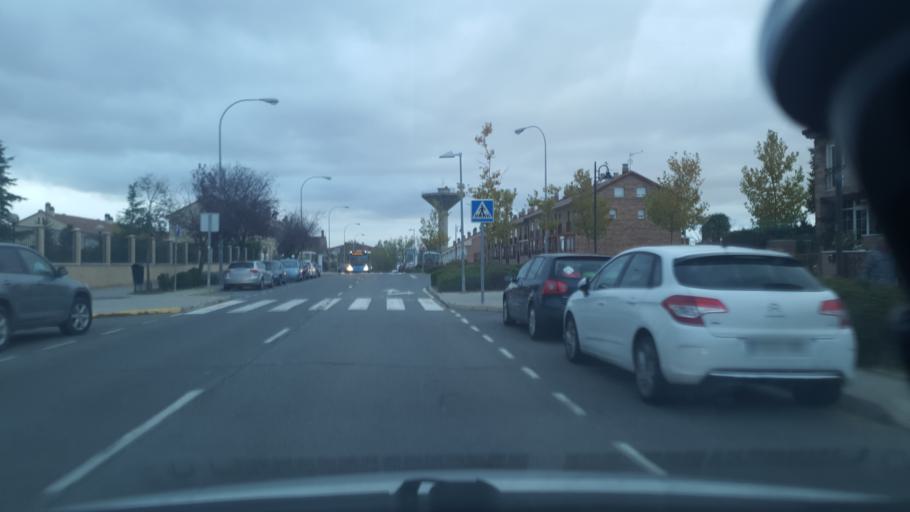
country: ES
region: Castille and Leon
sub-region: Provincia de Segovia
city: San Cristobal de Segovia
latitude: 40.9270
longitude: -4.0933
